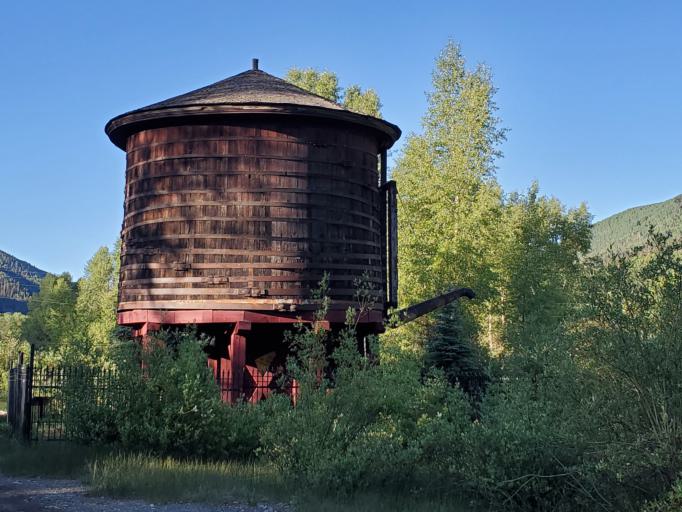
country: US
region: Colorado
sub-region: San Miguel County
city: Mountain Village
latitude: 37.6916
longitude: -108.0336
